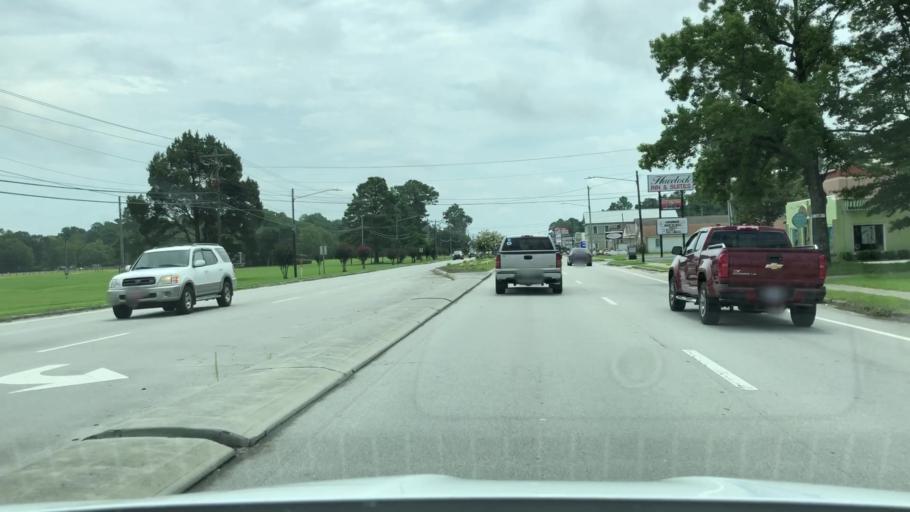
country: US
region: North Carolina
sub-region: Craven County
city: Havelock
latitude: 34.8753
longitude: -76.9034
